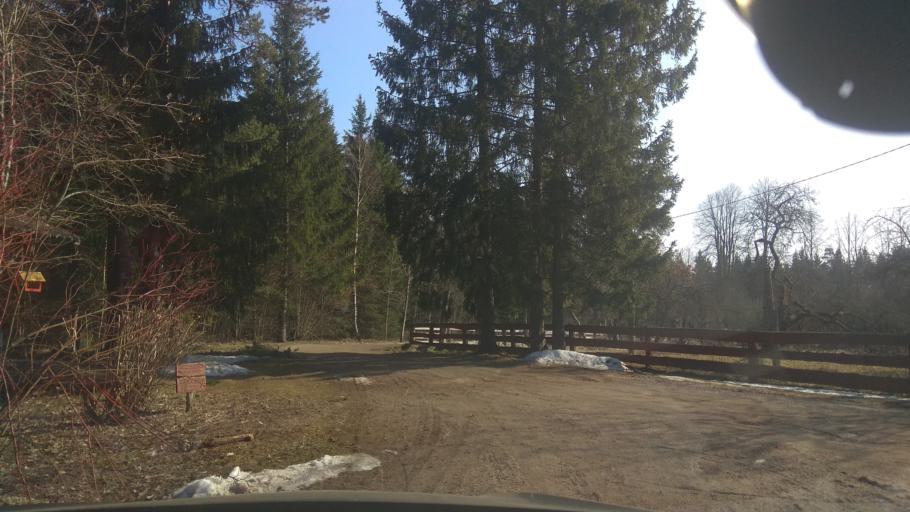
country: LT
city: Baltoji Voke
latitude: 54.4832
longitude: 25.2705
